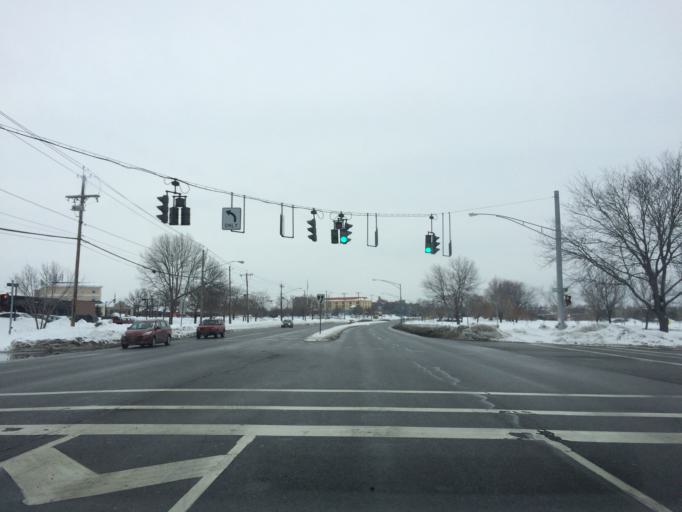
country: US
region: New York
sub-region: Monroe County
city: Rochester
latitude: 43.1026
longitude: -77.6150
